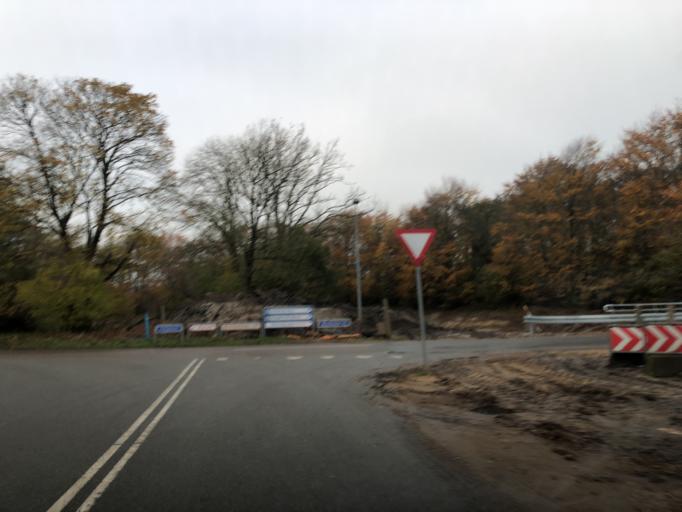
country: DK
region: Central Jutland
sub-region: Herning Kommune
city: Avlum
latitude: 56.2465
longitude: 8.8828
